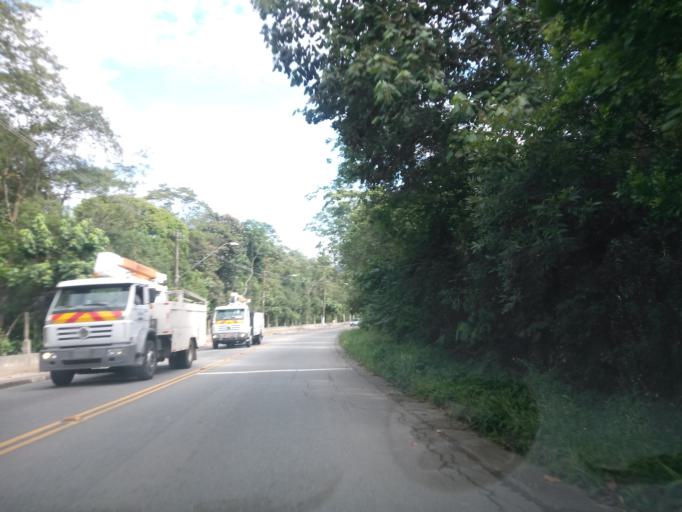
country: BR
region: Sao Paulo
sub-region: Sao Bernardo Do Campo
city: Sao Bernardo do Campo
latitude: -23.7971
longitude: -46.5436
